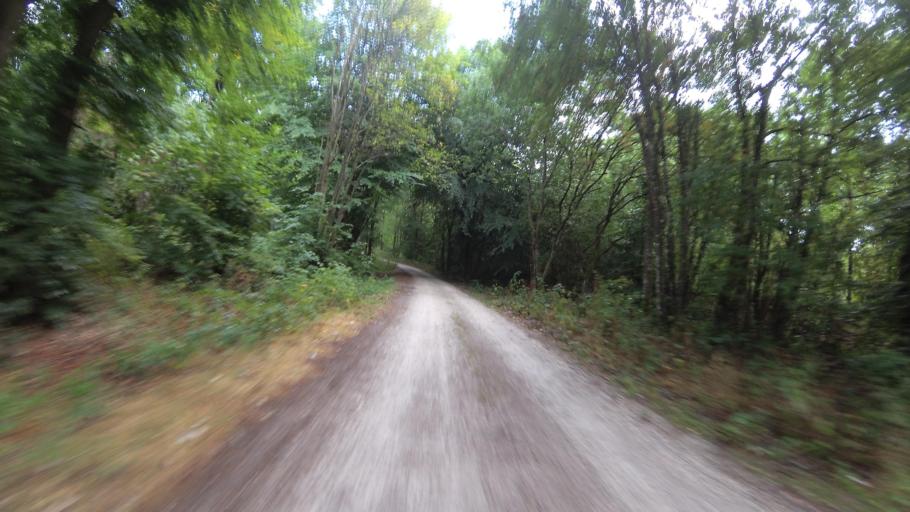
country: DE
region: Rheinland-Pfalz
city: Morbach
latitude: 49.7826
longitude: 7.1110
